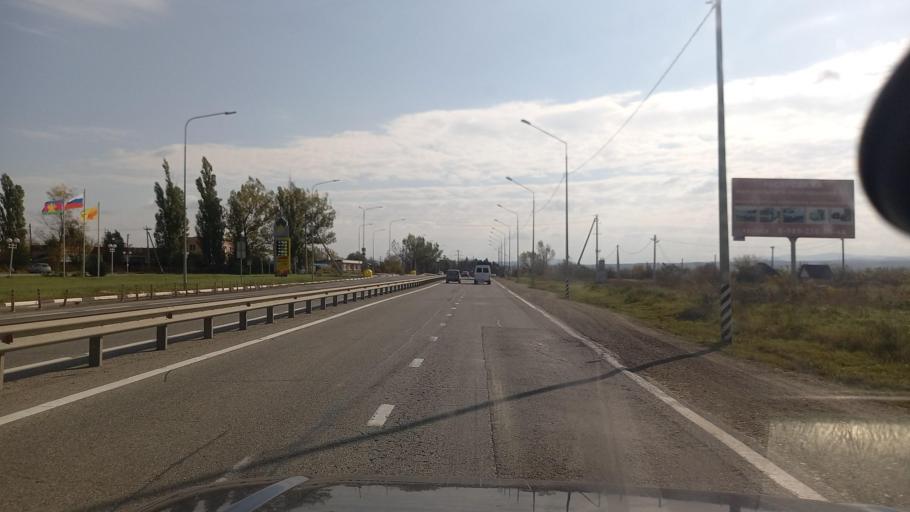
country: RU
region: Krasnodarskiy
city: Akhtyrskiy
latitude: 44.8485
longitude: 38.2765
